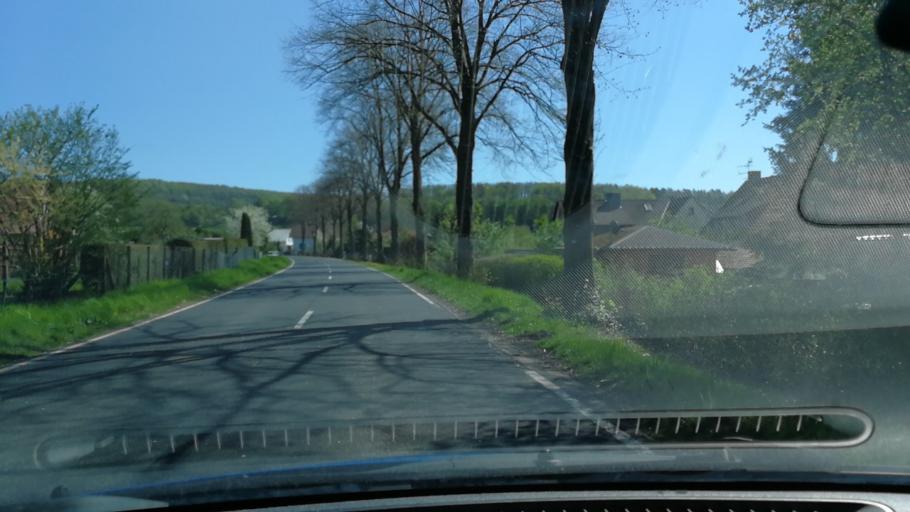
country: DE
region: Lower Saxony
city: Hardegsen
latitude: 51.6190
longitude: 9.7912
